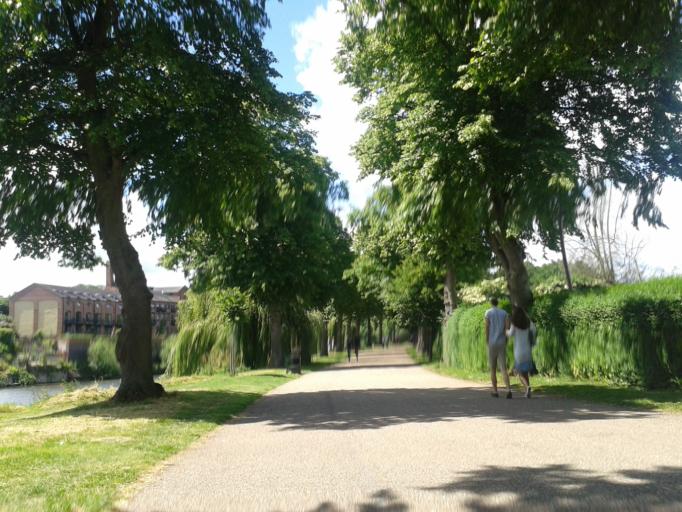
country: GB
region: England
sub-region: Shropshire
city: Shrewsbury
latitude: 52.7044
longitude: -2.7504
